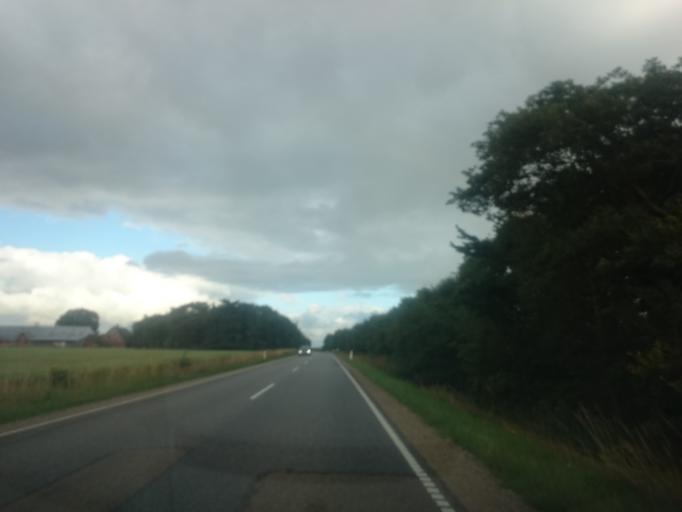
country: DK
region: South Denmark
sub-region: Billund Kommune
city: Grindsted
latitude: 55.6640
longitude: 8.7588
